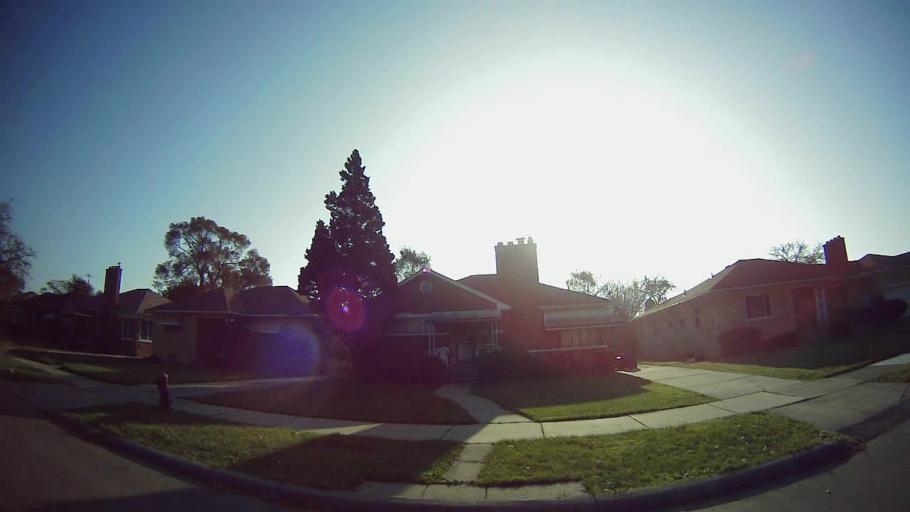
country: US
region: Michigan
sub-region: Wayne County
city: Dearborn
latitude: 42.3601
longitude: -83.1599
